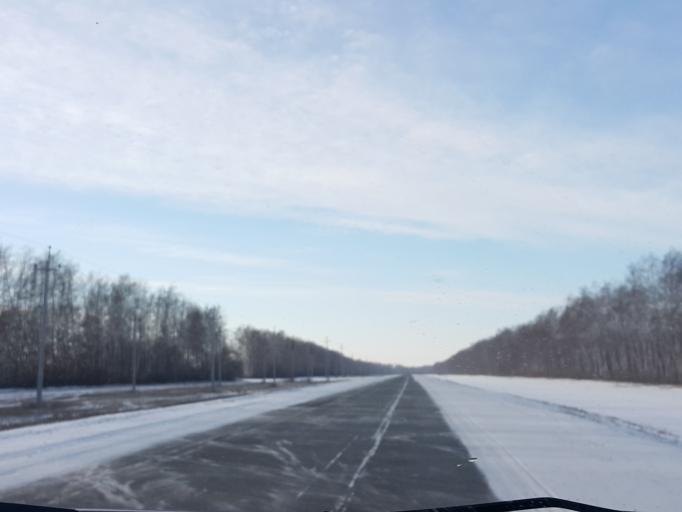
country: RU
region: Tambov
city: Znamenka
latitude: 52.3900
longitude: 41.3493
